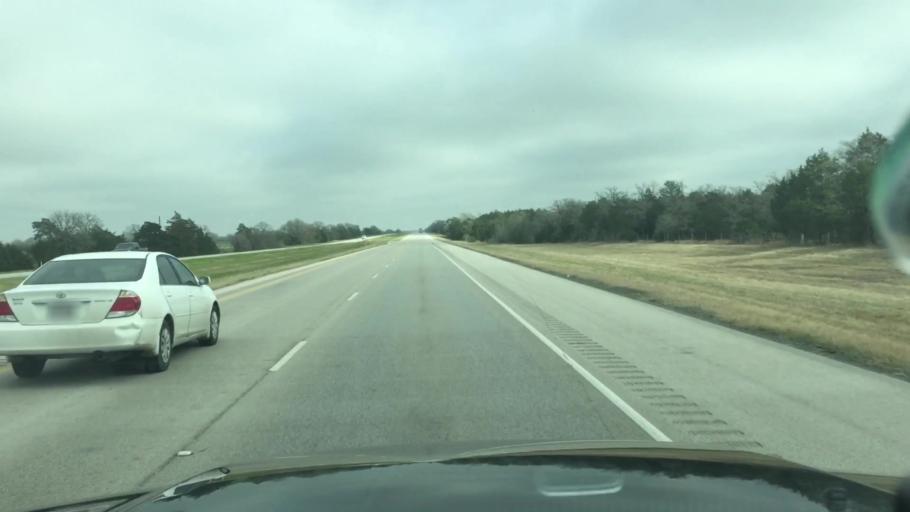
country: US
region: Texas
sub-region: Lee County
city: Giddings
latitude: 30.1438
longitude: -96.7346
